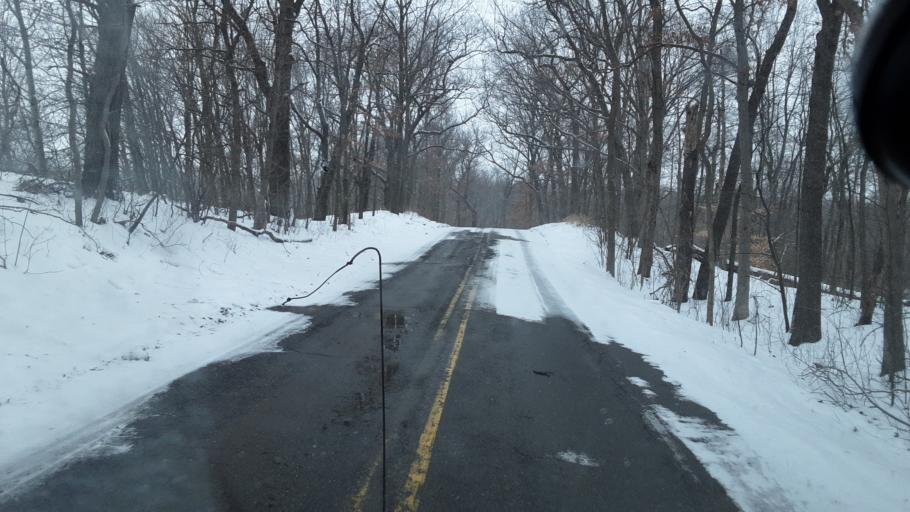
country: US
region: Michigan
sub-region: Ingham County
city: Leslie
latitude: 42.4888
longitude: -84.3655
